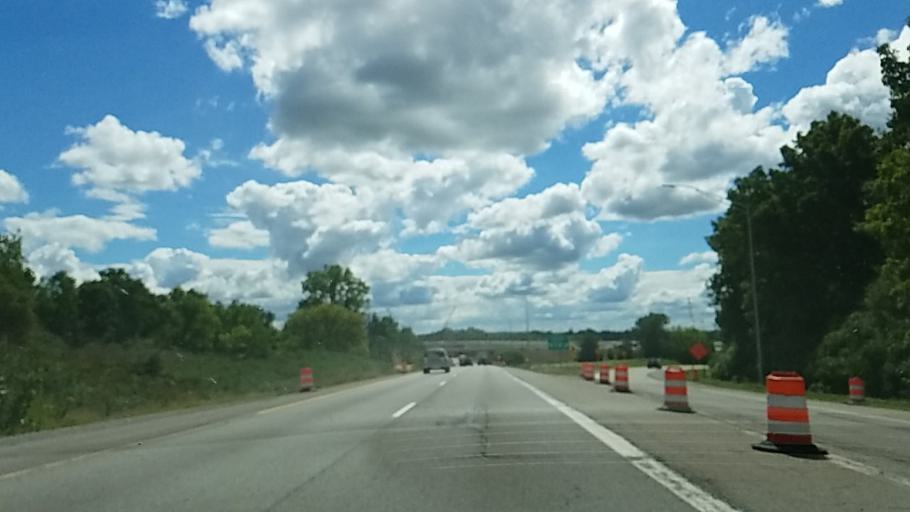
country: US
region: Michigan
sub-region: Livingston County
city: Brighton
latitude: 42.5293
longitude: -83.7544
